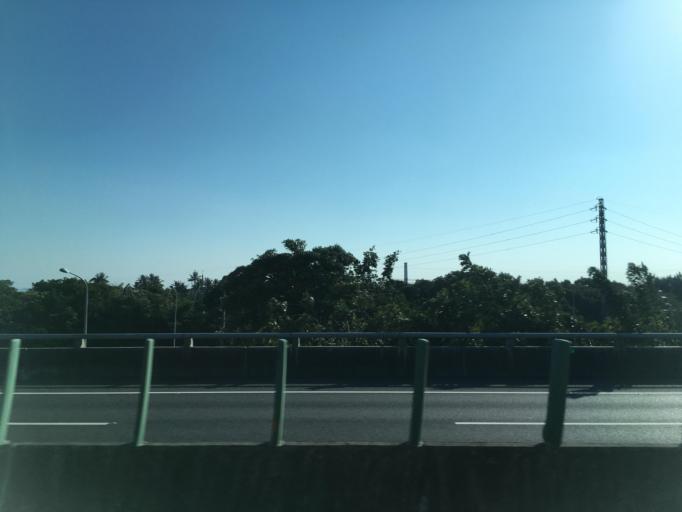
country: TW
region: Taiwan
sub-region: Chiayi
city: Taibao
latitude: 23.4191
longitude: 120.3843
